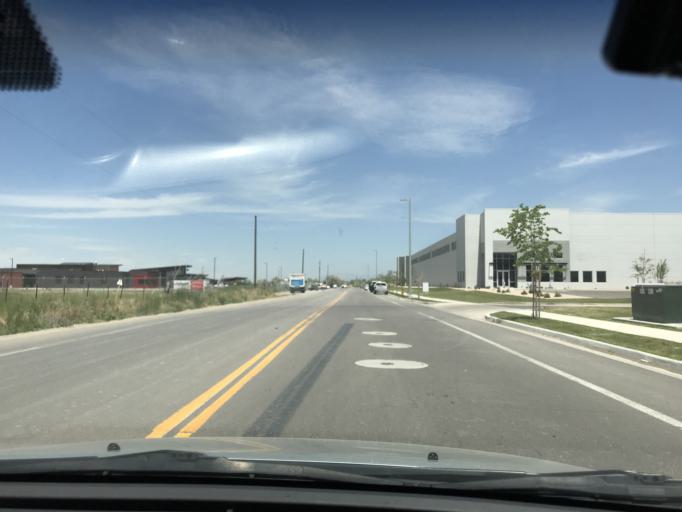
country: US
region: Utah
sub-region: Davis County
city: North Salt Lake
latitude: 40.8143
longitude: -111.9534
